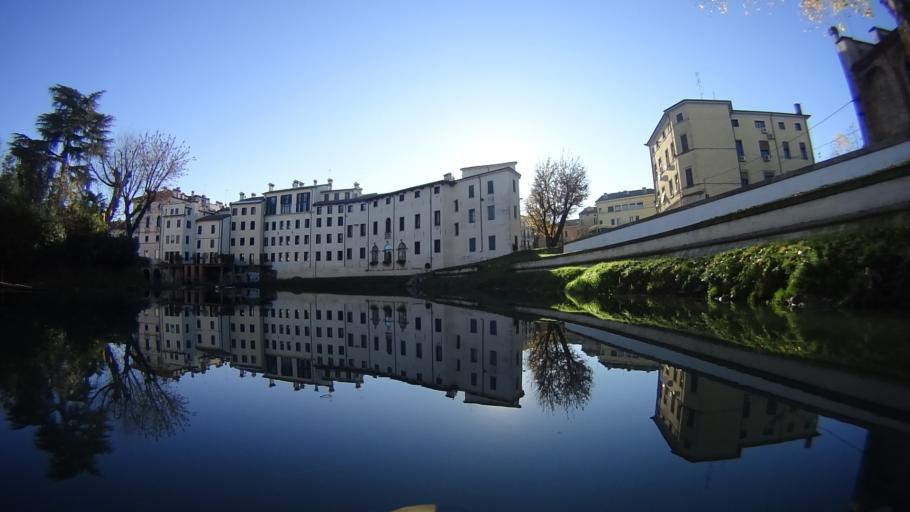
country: IT
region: Veneto
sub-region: Provincia di Vicenza
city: Vicenza
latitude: 45.5507
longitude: 11.5437
